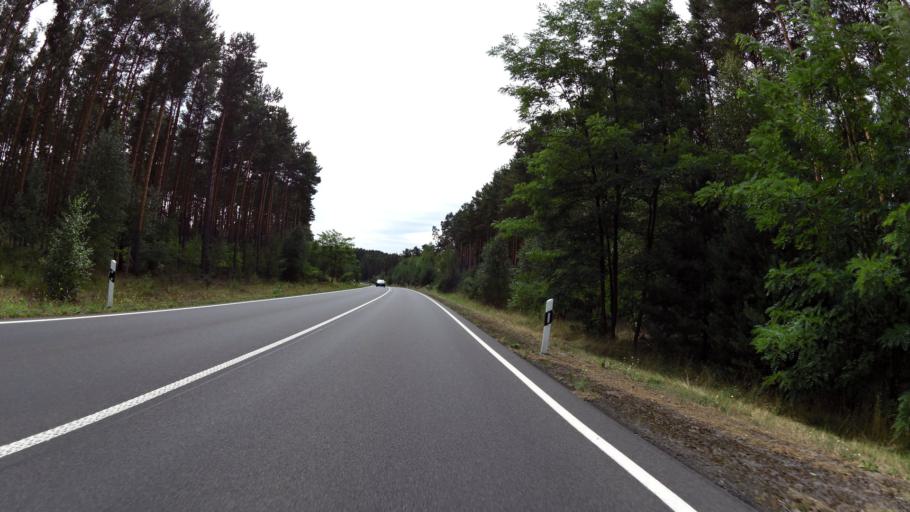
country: DE
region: Brandenburg
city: Schenkendobern
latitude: 51.9765
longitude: 14.6483
